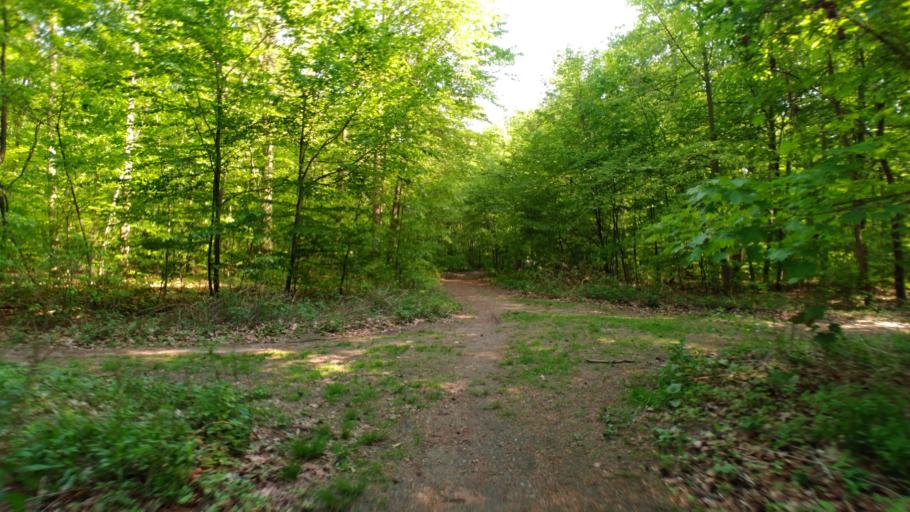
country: DE
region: Saxony
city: Albertstadt
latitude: 51.0758
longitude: 13.7961
